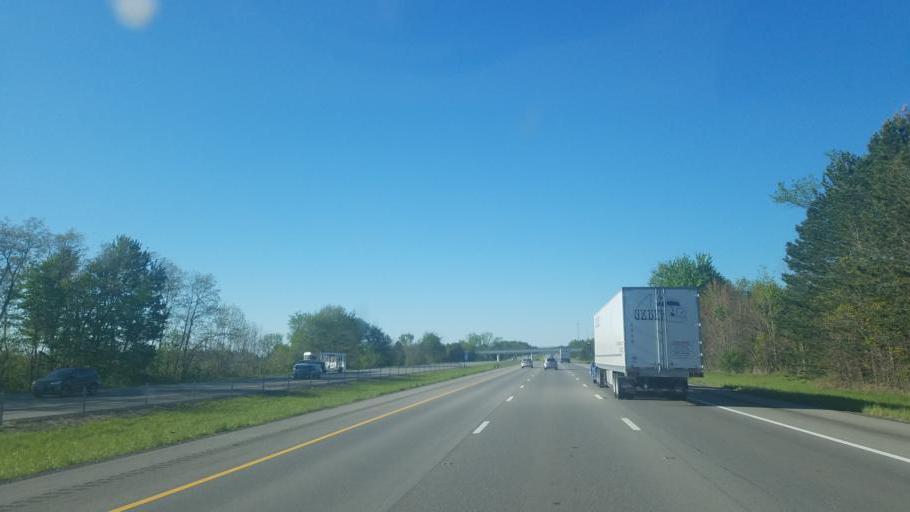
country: US
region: Ohio
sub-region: Morrow County
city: Cardington
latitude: 40.3956
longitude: -82.8229
